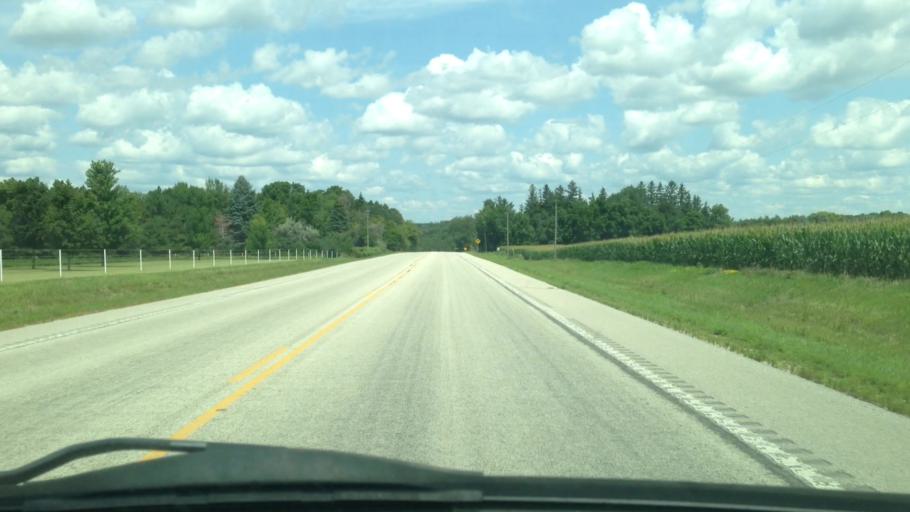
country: US
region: Minnesota
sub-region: Olmsted County
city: Rochester
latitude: 43.9668
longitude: -92.5183
